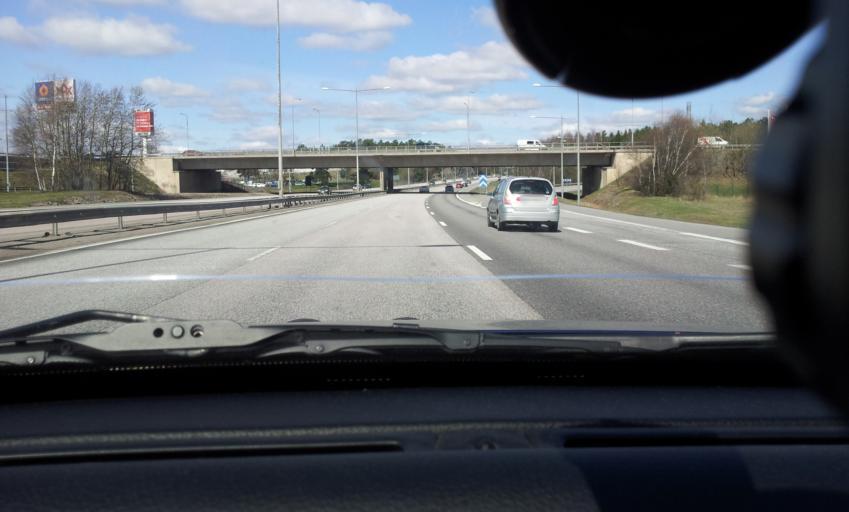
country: SE
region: Stockholm
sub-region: Haninge Kommun
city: Handen
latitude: 59.1988
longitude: 18.1331
